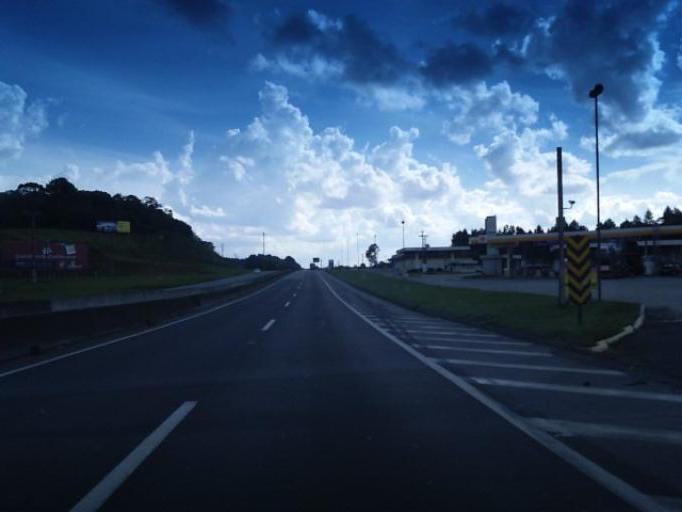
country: BR
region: Parana
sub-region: Campina Grande Do Sul
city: Campina Grande do Sul
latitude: -25.3272
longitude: -49.0282
